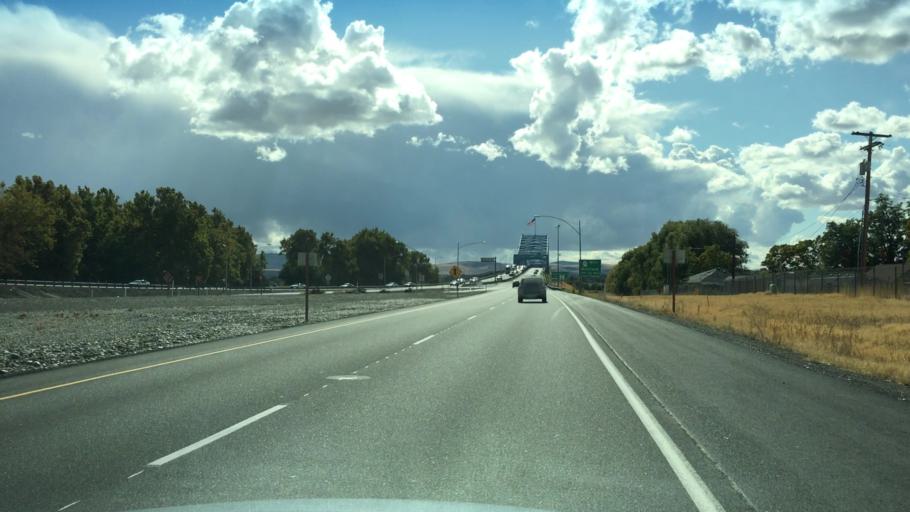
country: US
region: Washington
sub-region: Benton County
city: Kennewick
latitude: 46.2319
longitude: -119.1330
